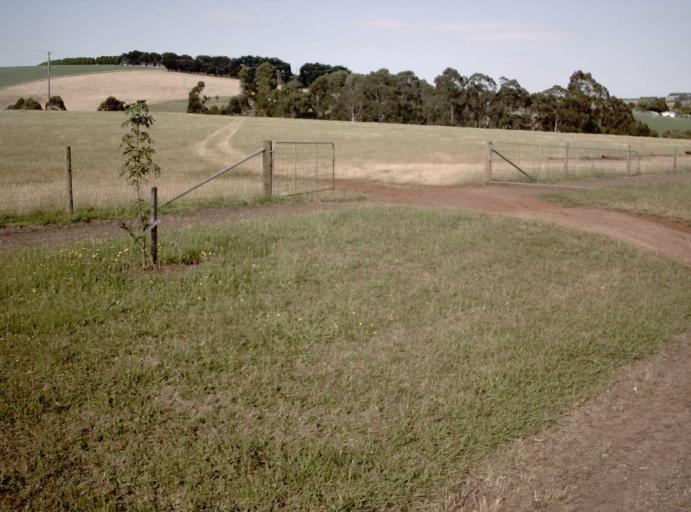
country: AU
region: Victoria
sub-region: Latrobe
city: Moe
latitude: -38.2888
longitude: 146.1862
